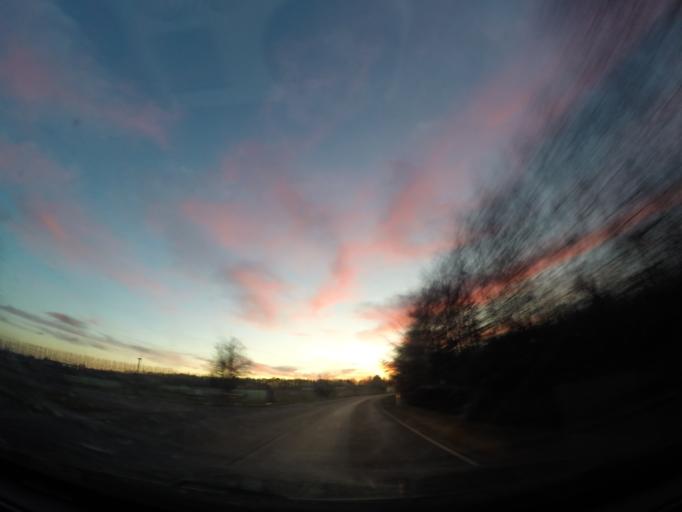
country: DK
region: Capital Region
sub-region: Hoje-Taastrup Kommune
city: Taastrup
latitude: 55.6684
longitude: 12.2856
